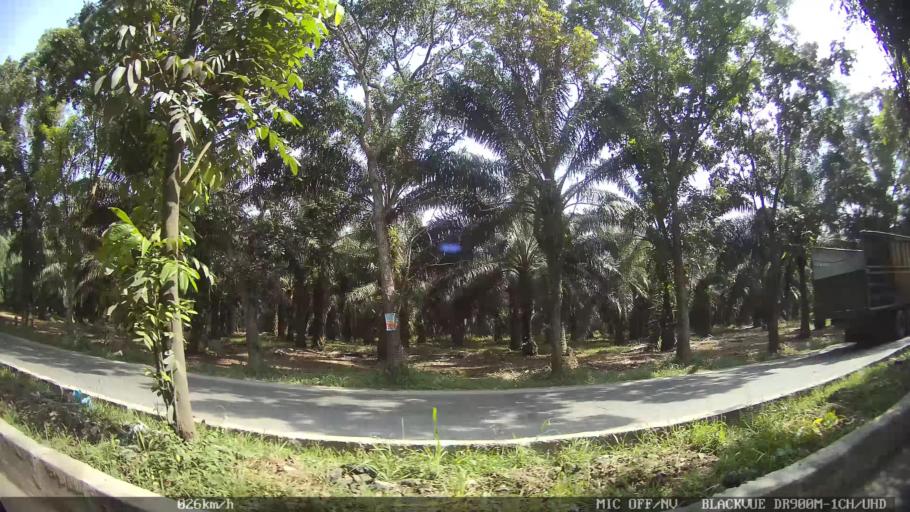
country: ID
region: North Sumatra
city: Binjai
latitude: 3.6508
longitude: 98.5220
